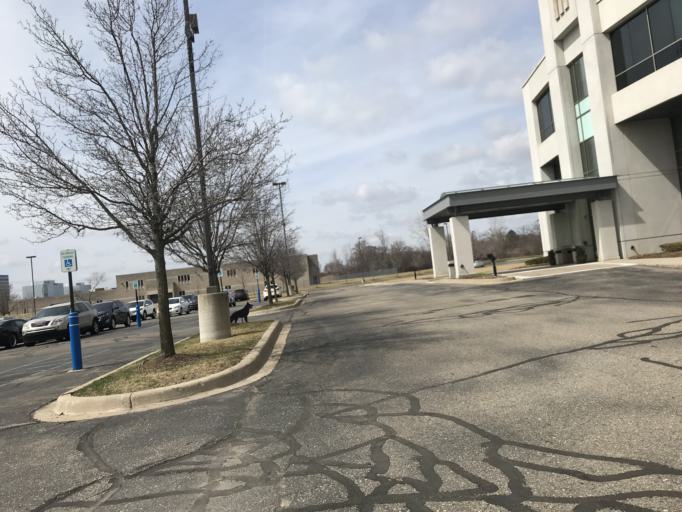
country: US
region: Michigan
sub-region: Oakland County
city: Franklin
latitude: 42.4907
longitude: -83.3043
